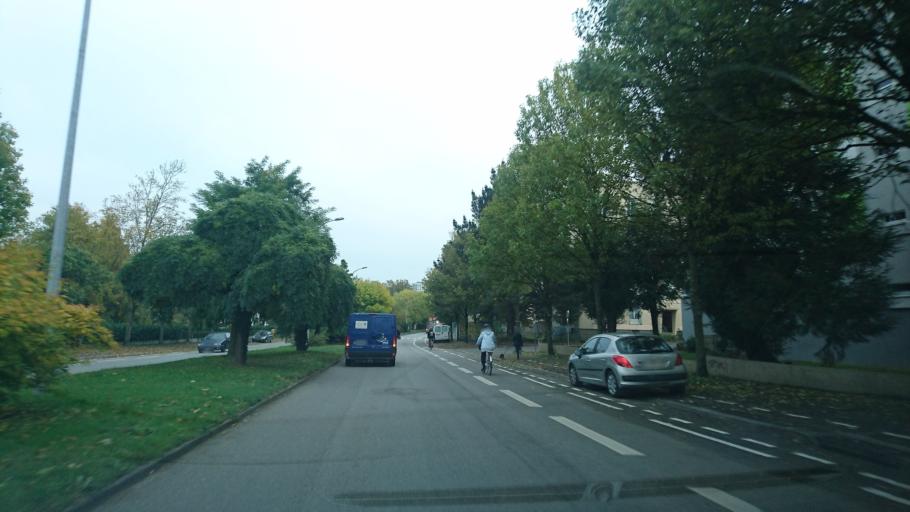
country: FR
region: Brittany
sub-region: Departement d'Ille-et-Vilaine
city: Rennes
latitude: 48.1155
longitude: -1.7042
